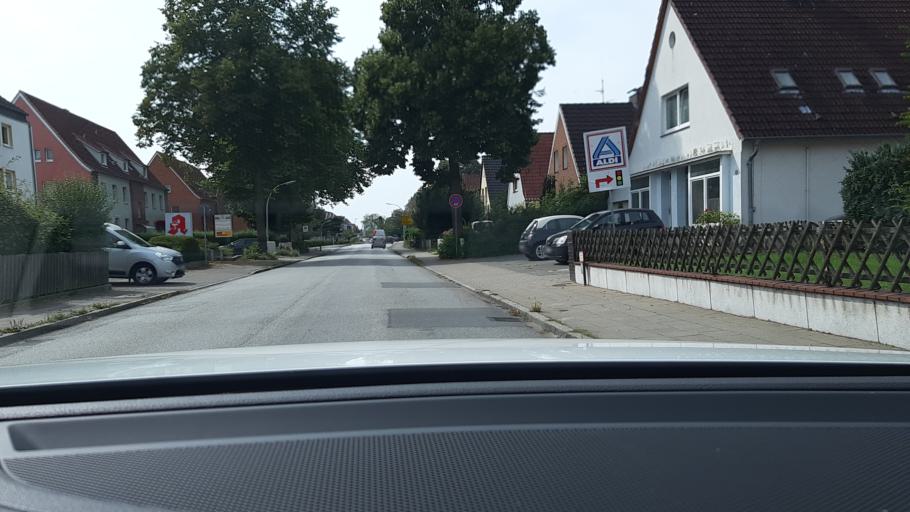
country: DE
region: Schleswig-Holstein
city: Bad Schwartau
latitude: 53.9054
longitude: 10.6724
